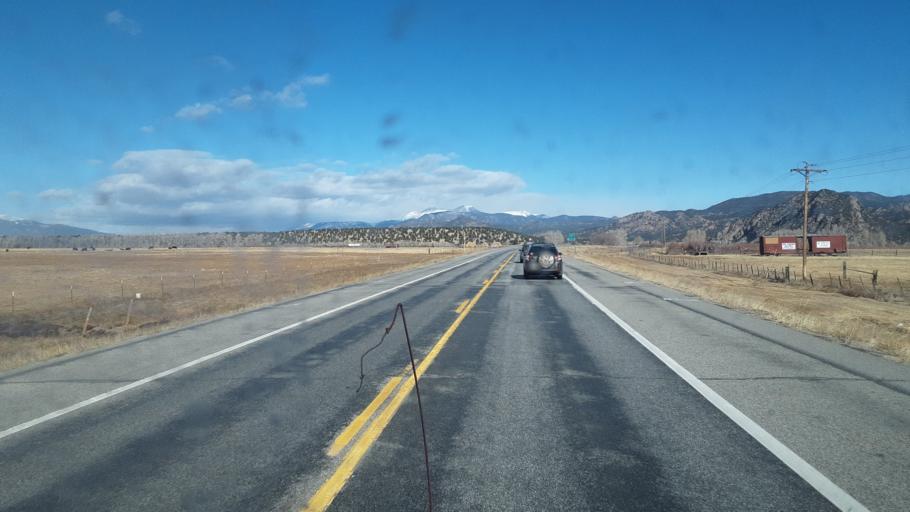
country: US
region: Colorado
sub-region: Chaffee County
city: Buena Vista
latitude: 38.7330
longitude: -106.0859
